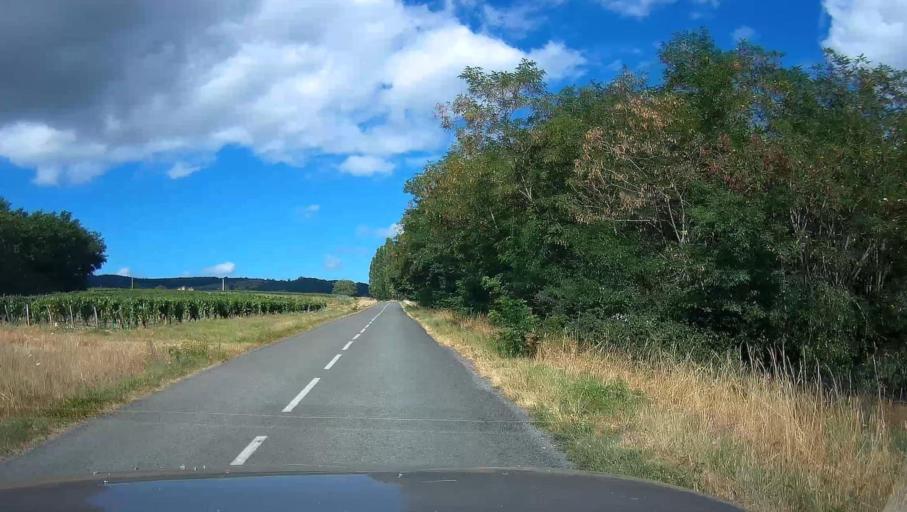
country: FR
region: Rhone-Alpes
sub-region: Departement du Rhone
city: Cogny
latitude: 45.9742
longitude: 4.6232
